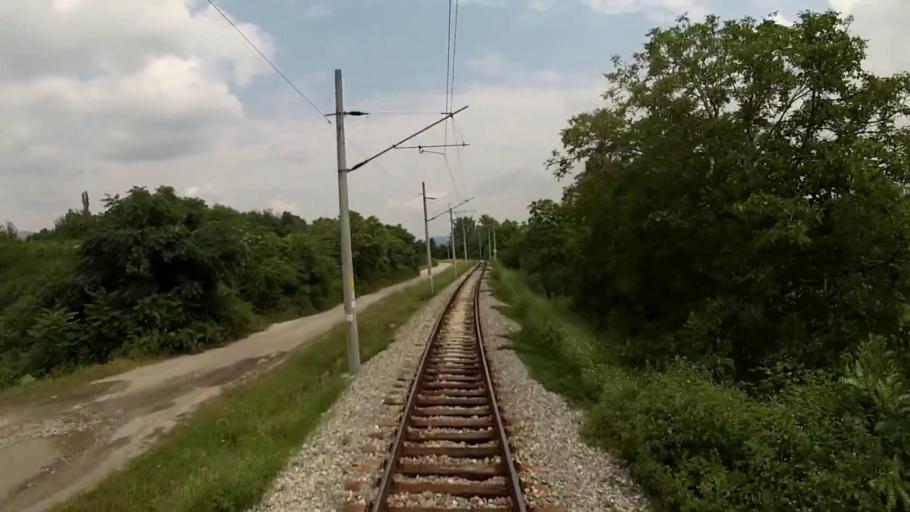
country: BG
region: Blagoevgrad
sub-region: Obshtina Simitli
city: Simitli
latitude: 41.8468
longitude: 23.1430
